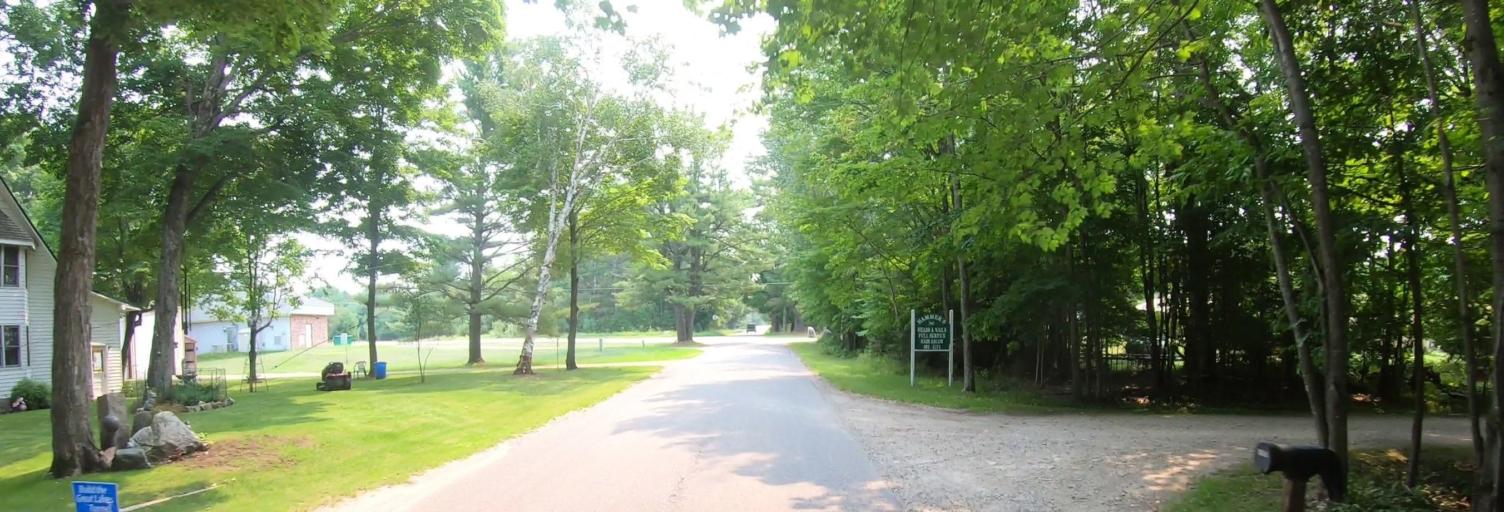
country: CA
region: Ontario
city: Thessalon
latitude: 46.0170
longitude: -83.7436
